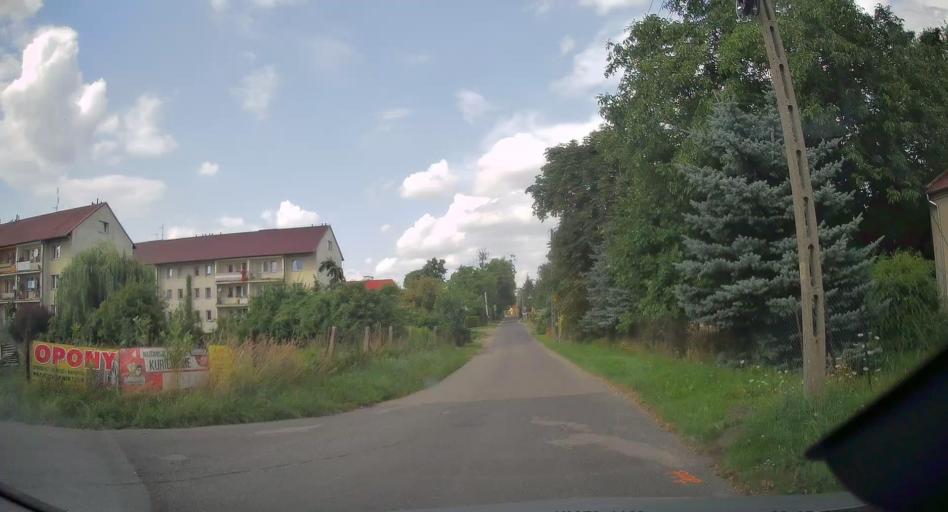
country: PL
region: Lodz Voivodeship
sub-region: Powiat brzezinski
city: Rogow
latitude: 51.8175
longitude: 19.8975
